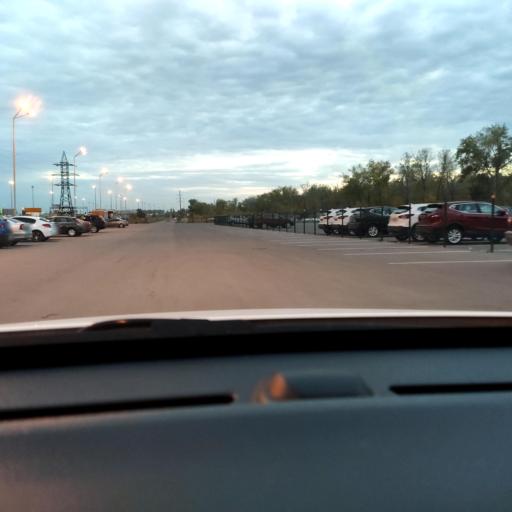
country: RU
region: Voronezj
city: Somovo
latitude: 51.6617
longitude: 39.3008
